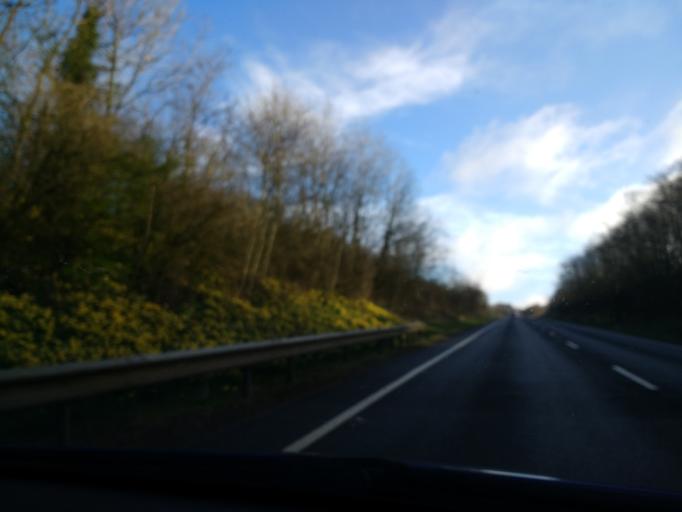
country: GB
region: England
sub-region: Cumbria
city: Cockermouth
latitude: 54.6708
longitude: -3.3875
